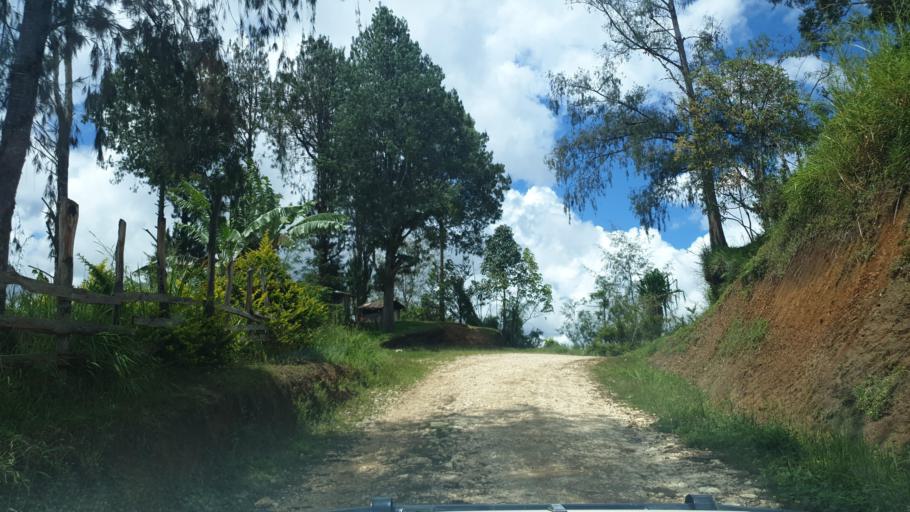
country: PG
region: Chimbu
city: Kundiawa
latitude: -6.2190
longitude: 145.1377
